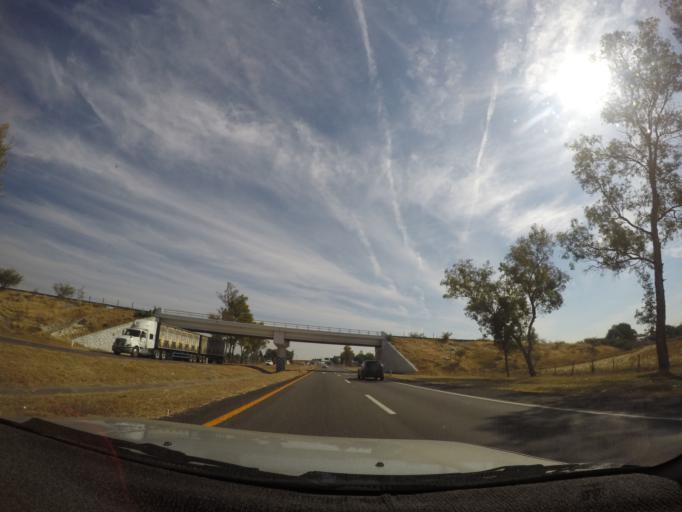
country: MX
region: Michoacan
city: Vistahermosa de Negrete
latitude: 20.3034
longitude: -102.4864
